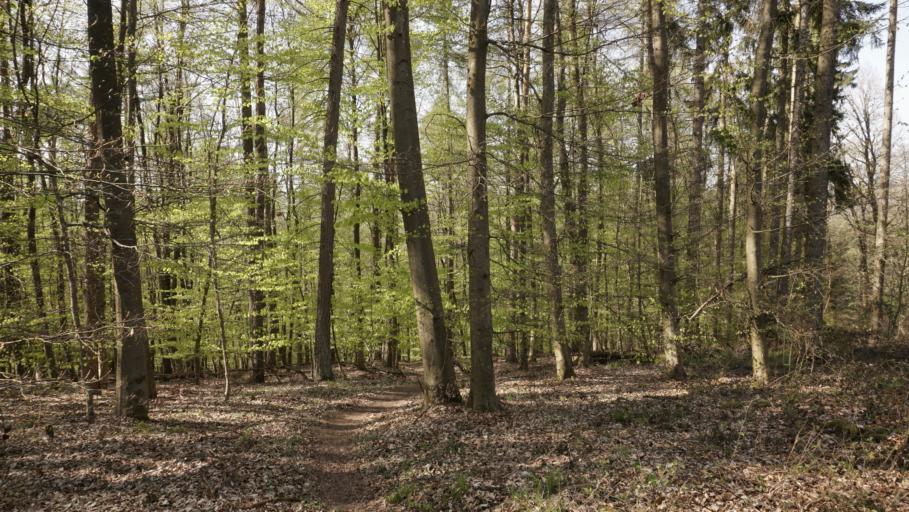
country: DE
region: Baden-Wuerttemberg
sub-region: Karlsruhe Region
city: Neckargerach
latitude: 49.4004
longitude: 9.0890
